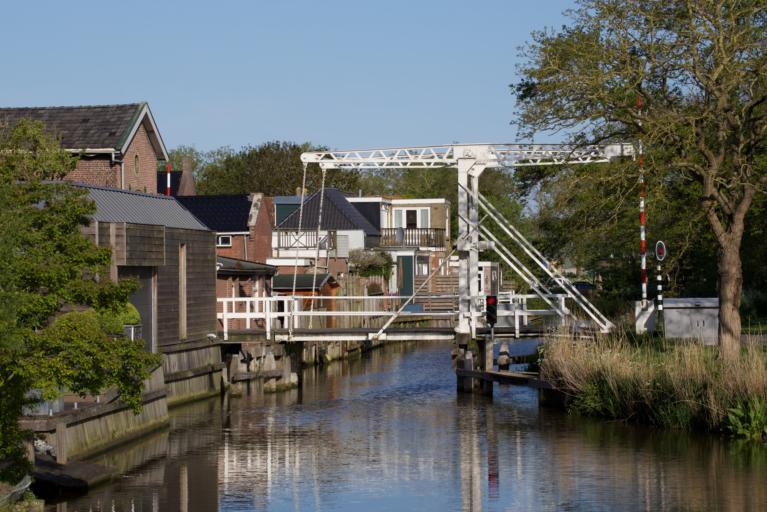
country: NL
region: Friesland
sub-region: Sudwest Fryslan
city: Bolsward
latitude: 53.0625
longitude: 5.5174
